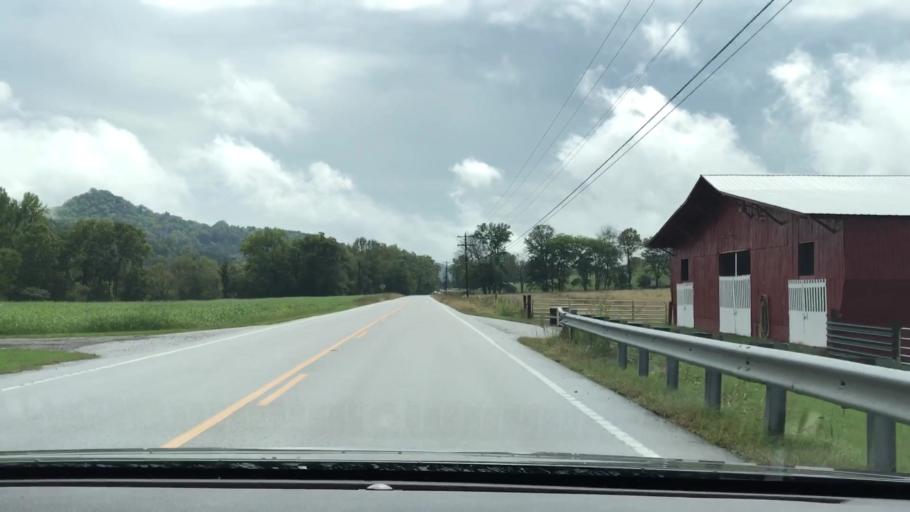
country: US
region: Tennessee
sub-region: Smith County
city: Carthage
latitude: 36.3474
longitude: -85.9653
